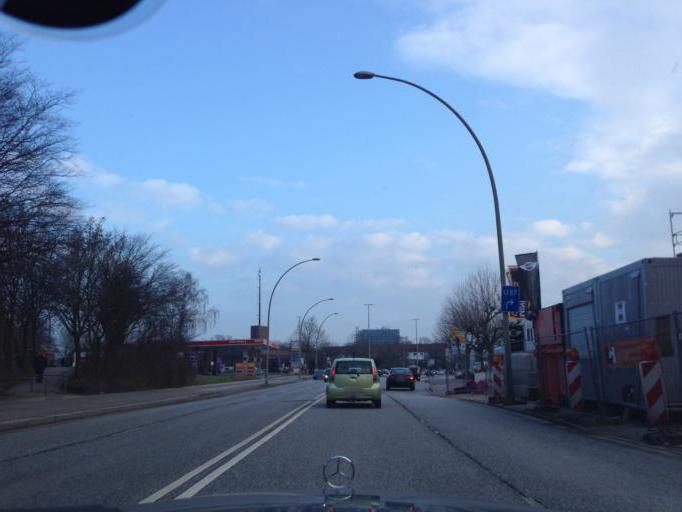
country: DE
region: Hamburg
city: Bergedorf
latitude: 53.4920
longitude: 10.2005
